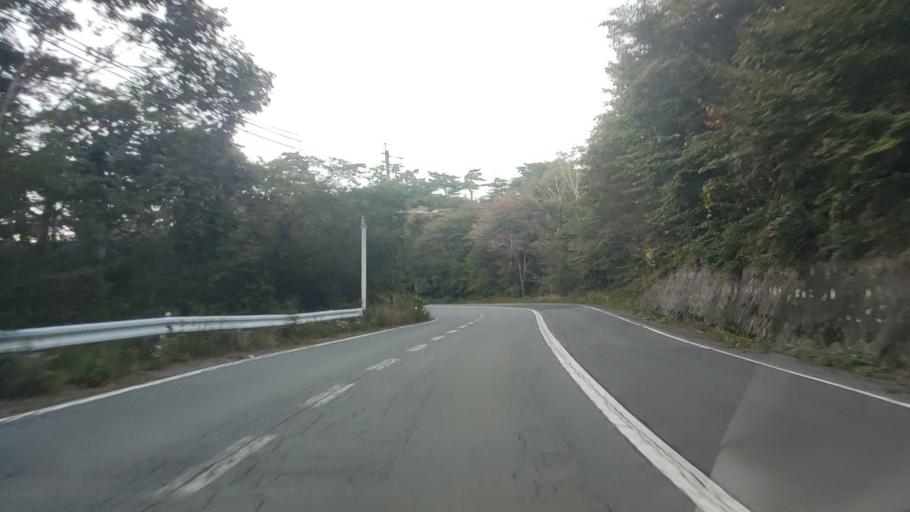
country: JP
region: Nagano
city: Komoro
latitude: 36.3920
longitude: 138.5819
